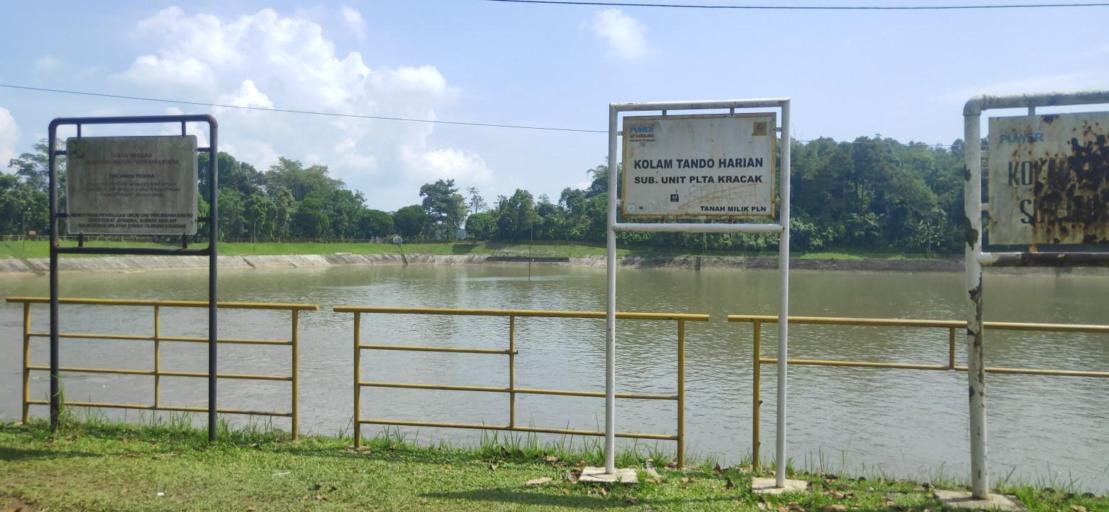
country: ID
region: West Java
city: Ciampea
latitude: -6.6265
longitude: 106.6374
